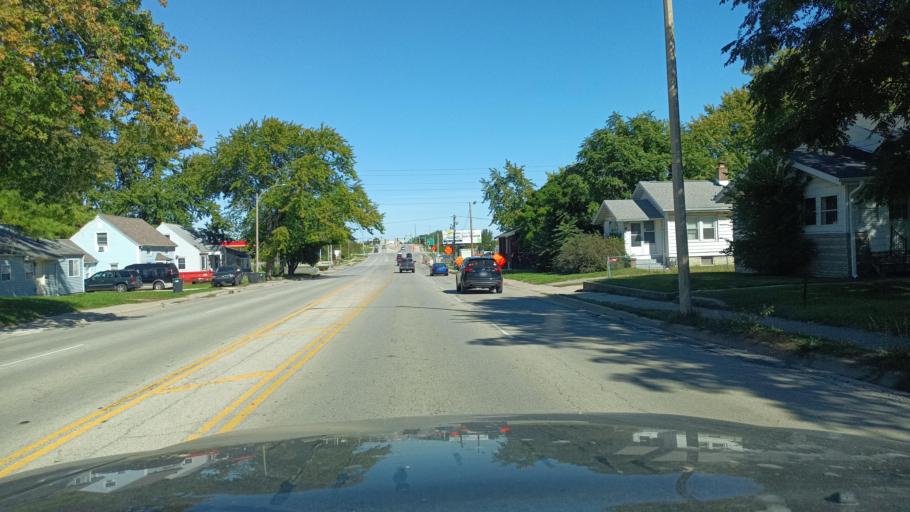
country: US
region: Illinois
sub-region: Champaign County
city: Champaign
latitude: 40.1298
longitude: -88.2436
